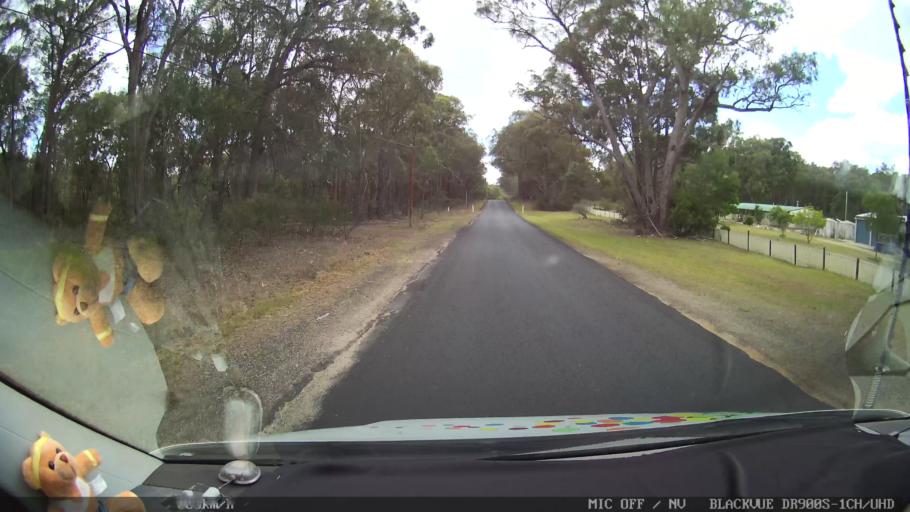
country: AU
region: New South Wales
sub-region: Glen Innes Severn
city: Glen Innes
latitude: -29.4328
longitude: 151.6343
